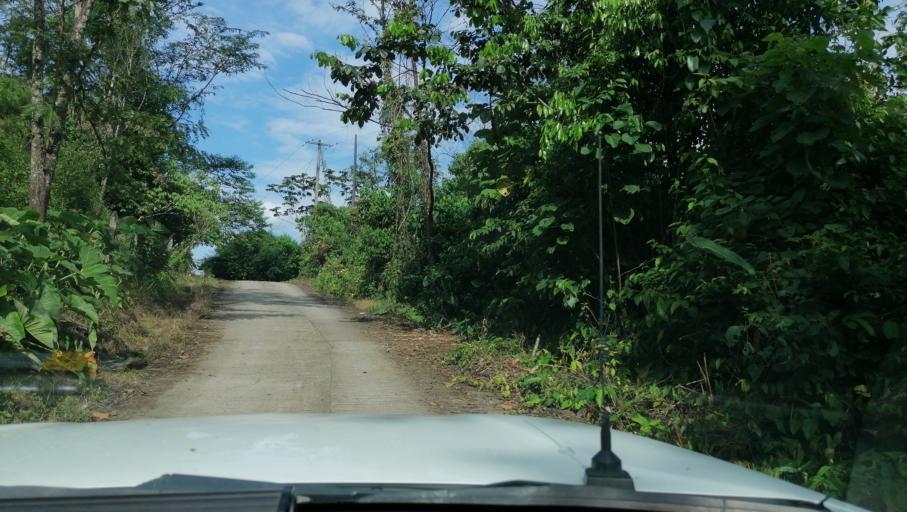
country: MX
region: Chiapas
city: Ostuacan
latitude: 17.4542
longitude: -93.2432
